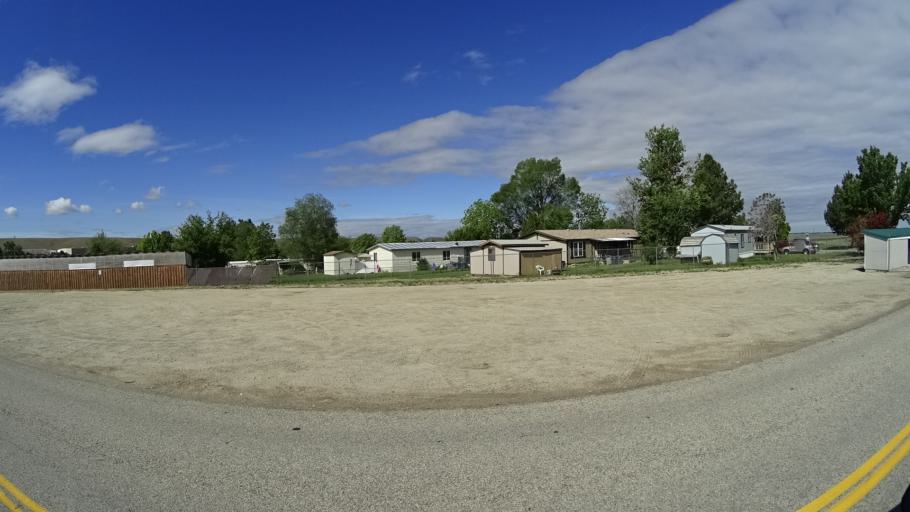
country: US
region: Idaho
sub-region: Ada County
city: Boise
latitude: 43.5274
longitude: -116.1553
